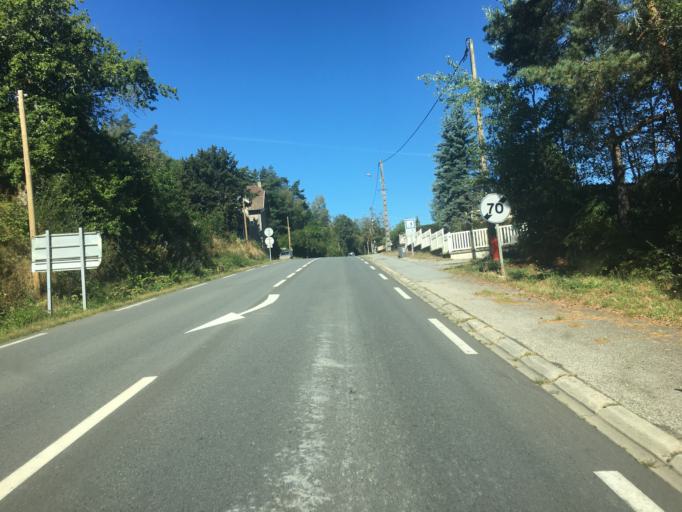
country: FR
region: Limousin
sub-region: Departement de la Correze
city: Bort-les-Orgues
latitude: 45.4105
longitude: 2.4839
